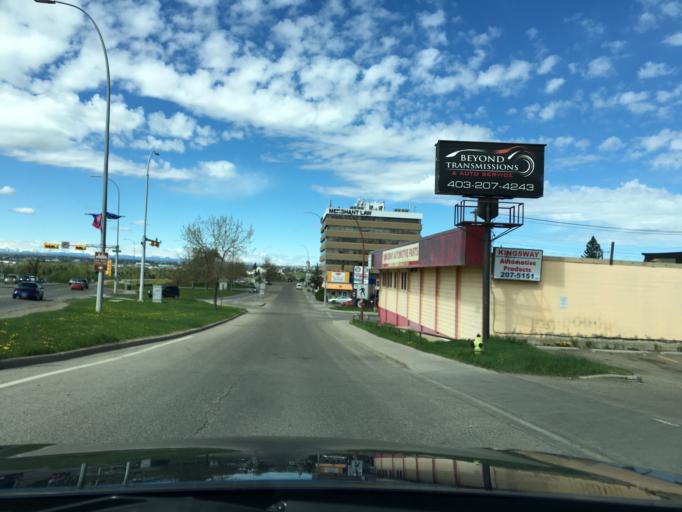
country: CA
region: Alberta
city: Calgary
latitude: 51.0378
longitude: -113.9946
